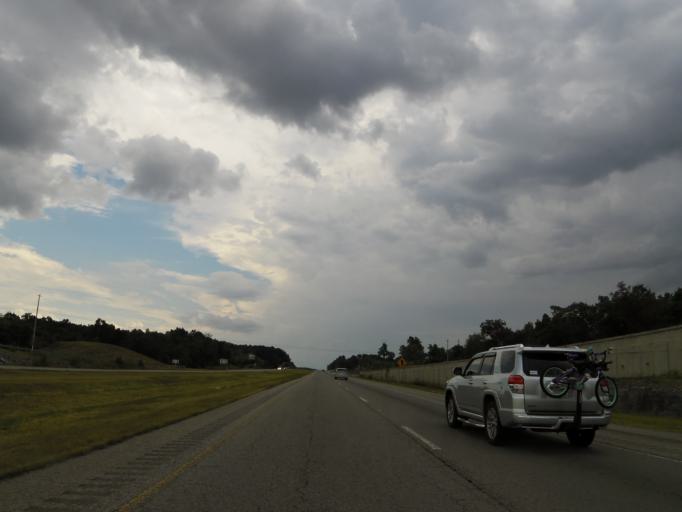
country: US
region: Tennessee
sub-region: Wilson County
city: Rural Hill
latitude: 36.0386
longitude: -86.4293
